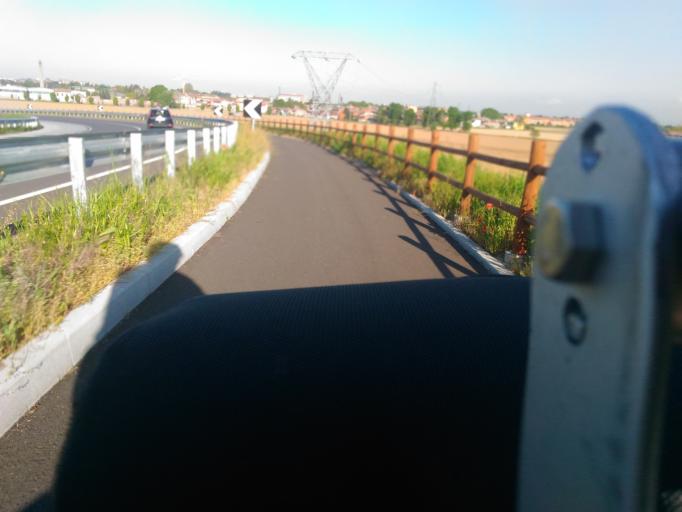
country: IT
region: Lombardy
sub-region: Citta metropolitana di Milano
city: Vizzolo Predabissi
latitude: 45.3551
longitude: 9.3578
